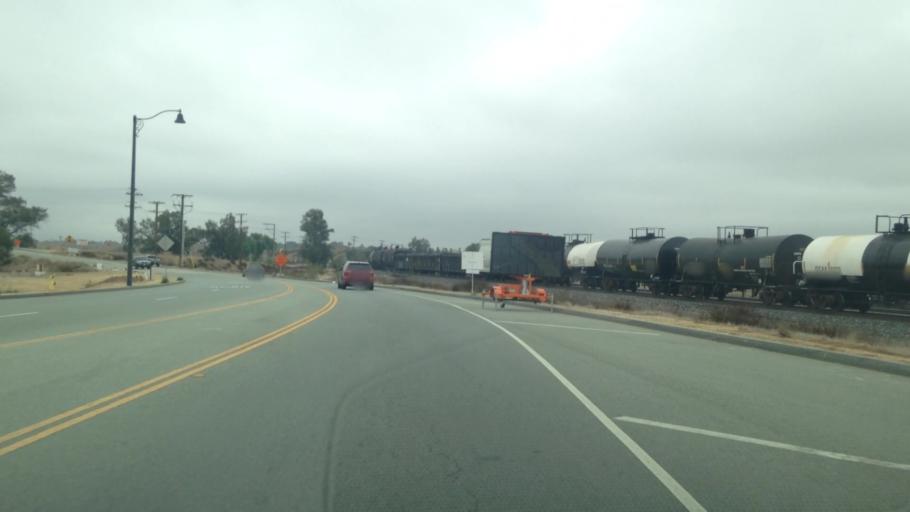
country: US
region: California
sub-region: Riverside County
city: Beaumont
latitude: 33.9438
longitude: -117.0072
